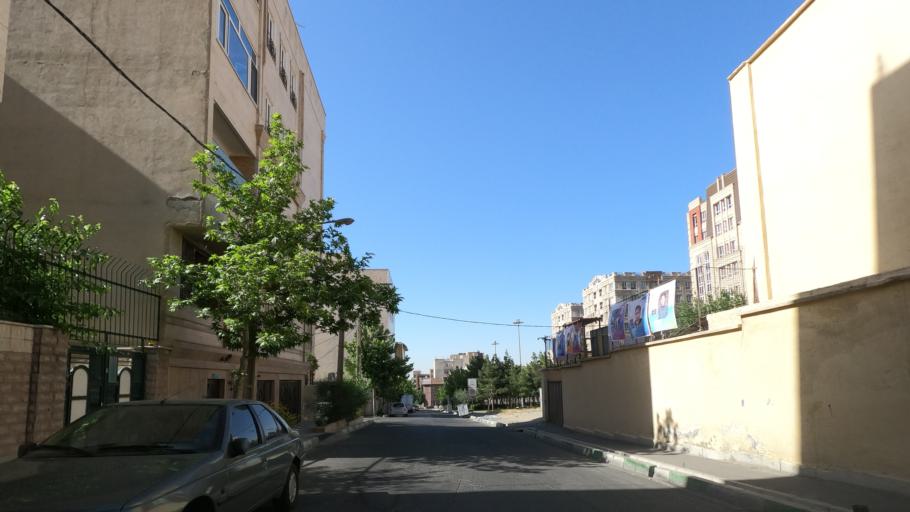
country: IR
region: Tehran
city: Tajrish
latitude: 35.7612
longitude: 51.3144
